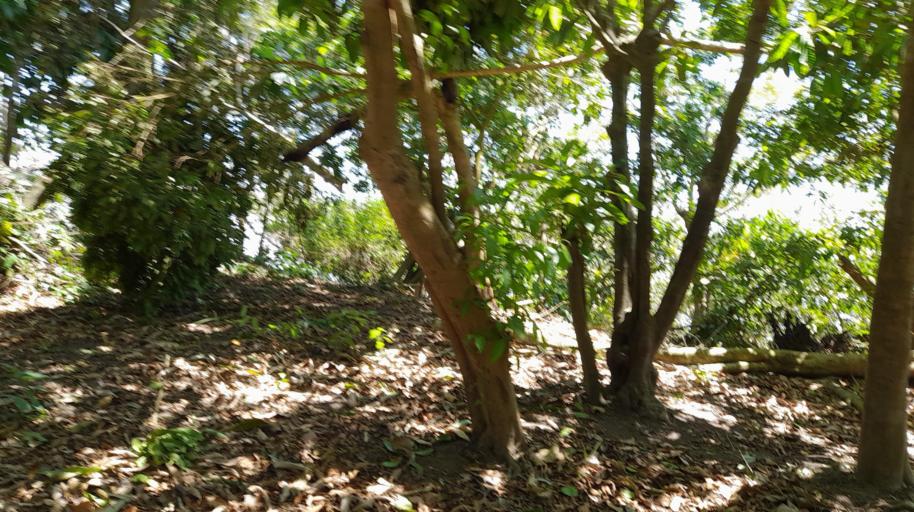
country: PE
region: Ucayali
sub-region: Provincia de Coronel Portillo
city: Puerto Callao
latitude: -8.2640
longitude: -74.6388
